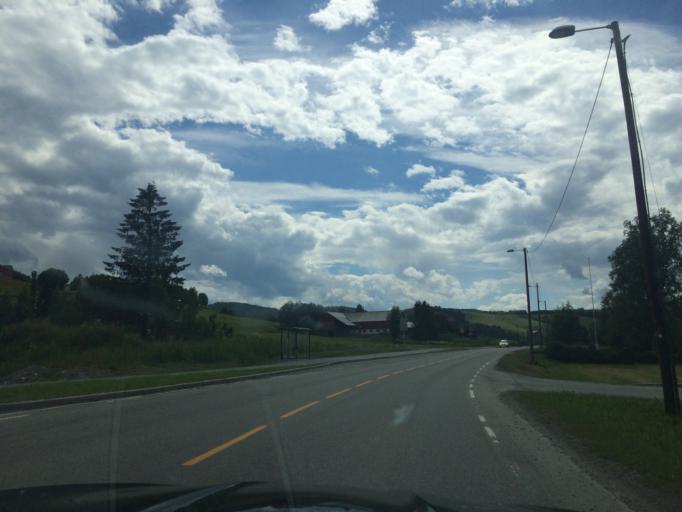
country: NO
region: Sor-Trondelag
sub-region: Selbu
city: Mebonden
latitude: 63.2498
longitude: 11.0945
